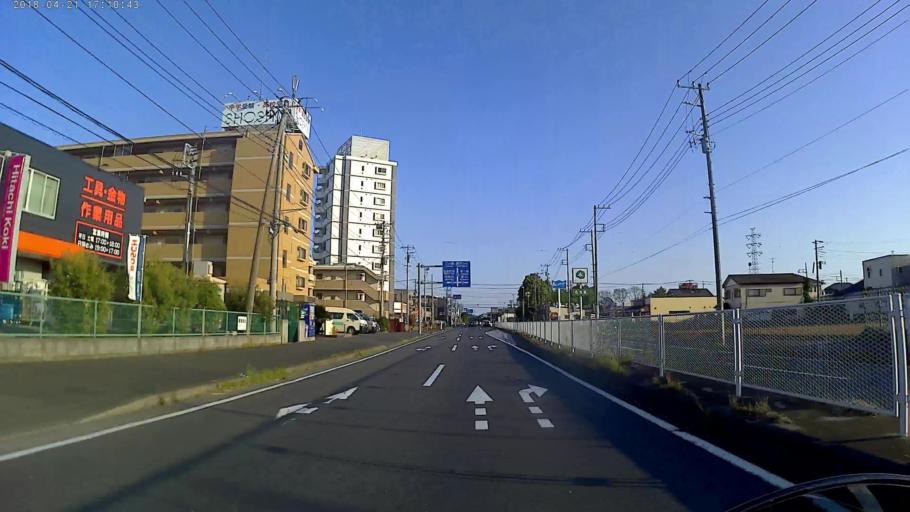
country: JP
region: Kanagawa
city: Fujisawa
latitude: 35.3939
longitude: 139.4439
